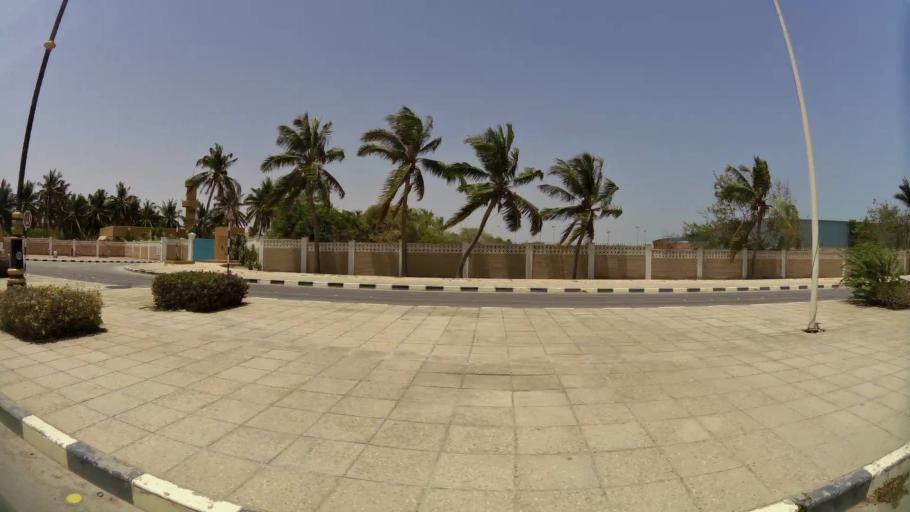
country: OM
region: Zufar
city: Salalah
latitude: 17.0263
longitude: 54.0905
